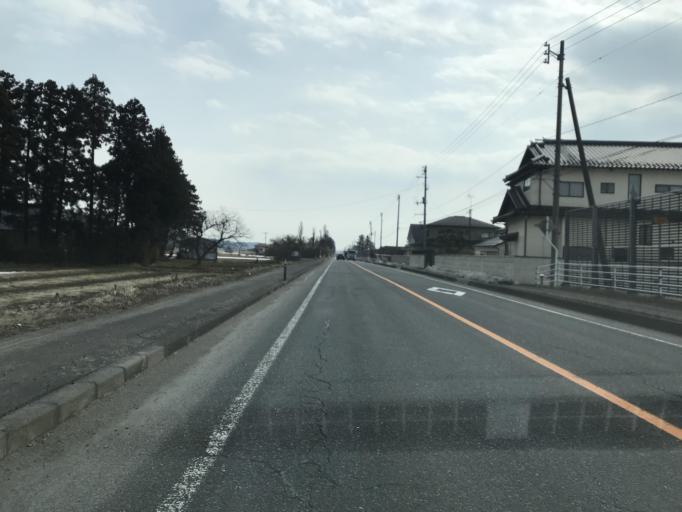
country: JP
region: Miyagi
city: Furukawa
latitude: 38.6916
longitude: 140.8478
